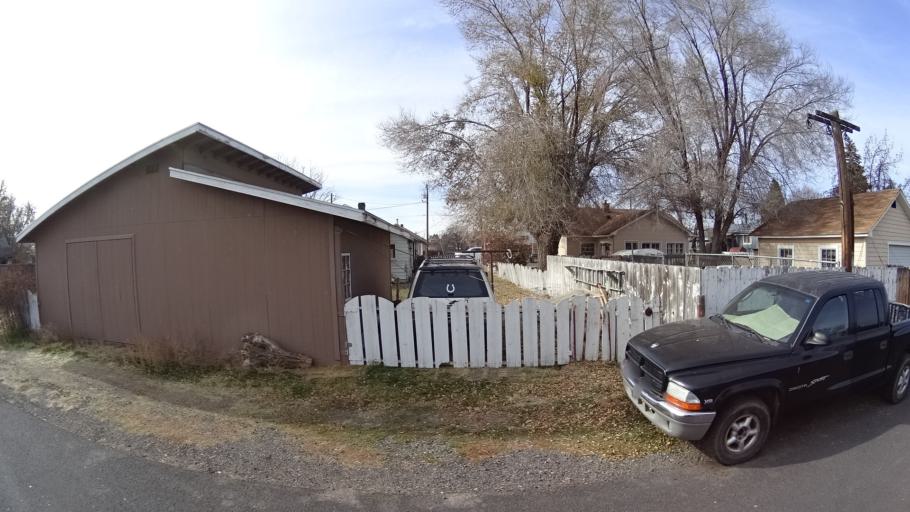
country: US
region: Oregon
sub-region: Klamath County
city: Klamath Falls
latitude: 41.9636
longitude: -121.9207
